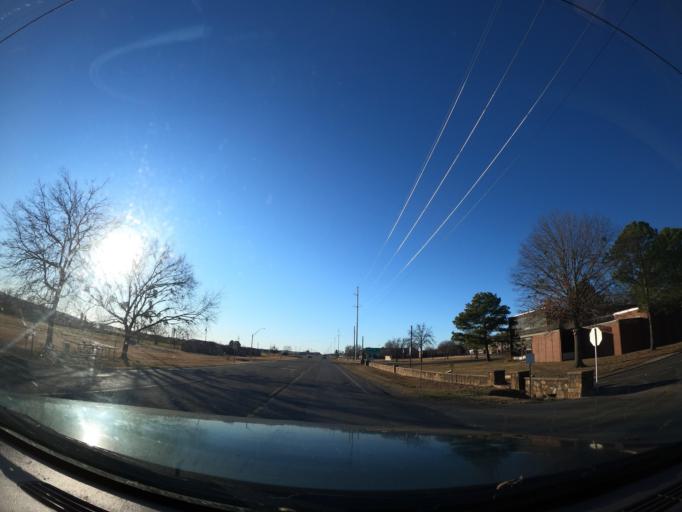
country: US
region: Oklahoma
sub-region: Latimer County
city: Wilburton
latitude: 34.9130
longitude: -95.3274
